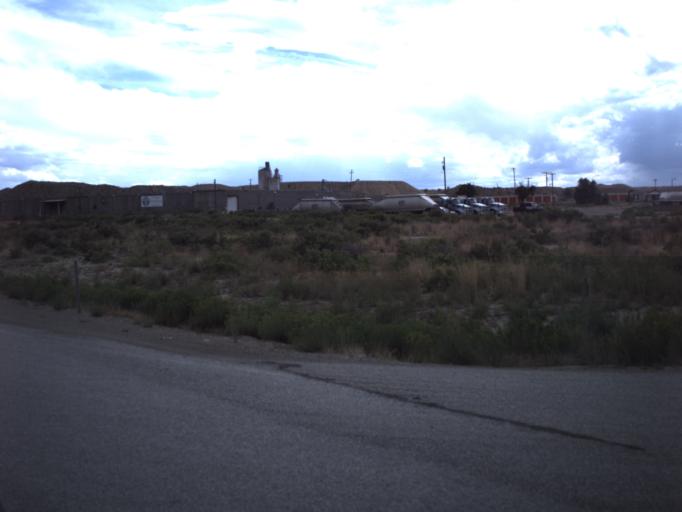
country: US
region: Utah
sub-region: Carbon County
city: Price
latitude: 39.5517
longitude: -110.8159
